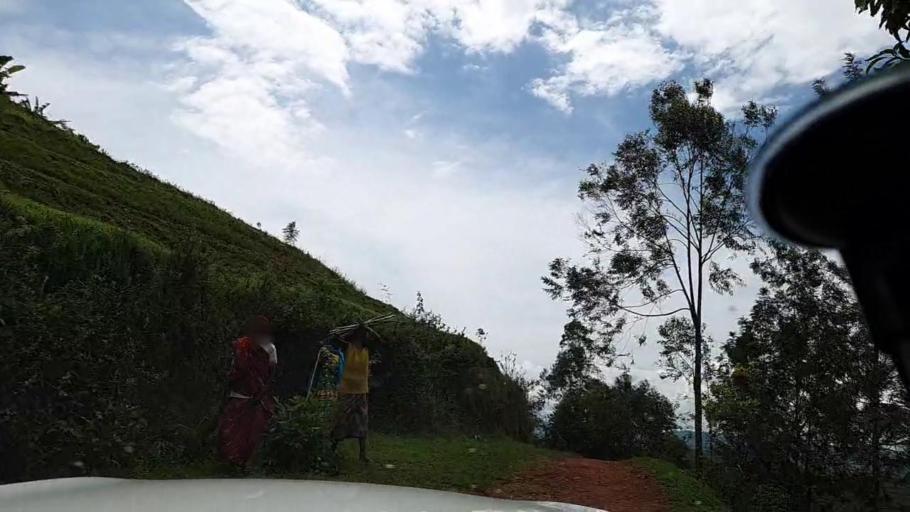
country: RW
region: Southern Province
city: Gitarama
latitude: -2.0695
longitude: 29.6455
